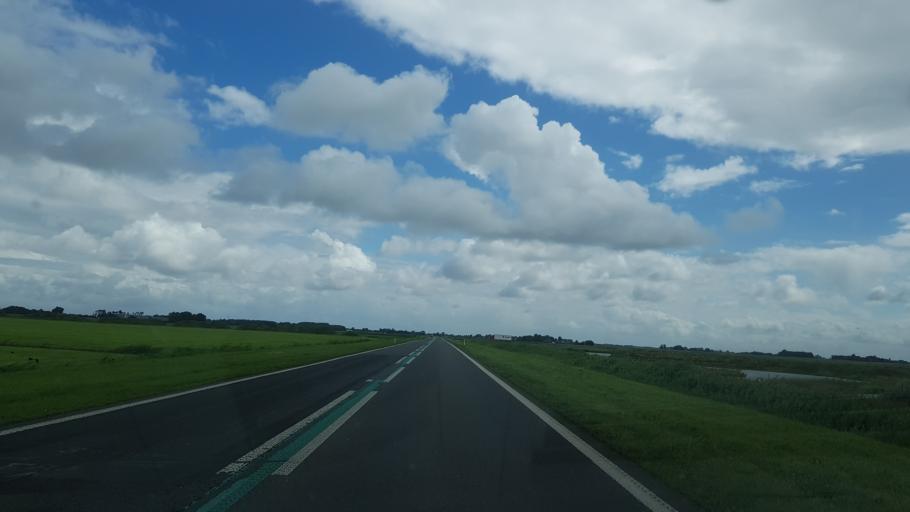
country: NL
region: Friesland
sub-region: Gemeente Dantumadiel
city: Walterswald
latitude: 53.3387
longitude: 6.0433
